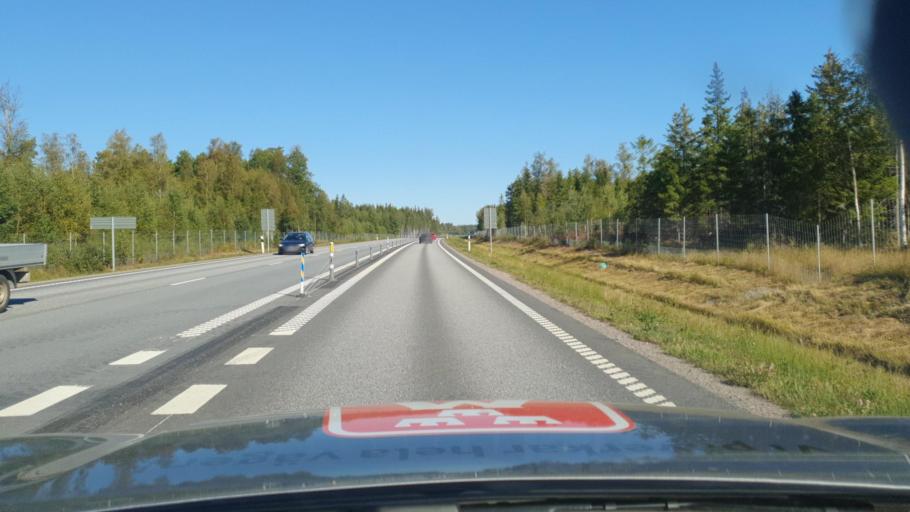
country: SE
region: OErebro
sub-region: Hallsbergs Kommun
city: Palsboda
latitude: 59.0713
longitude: 15.3113
